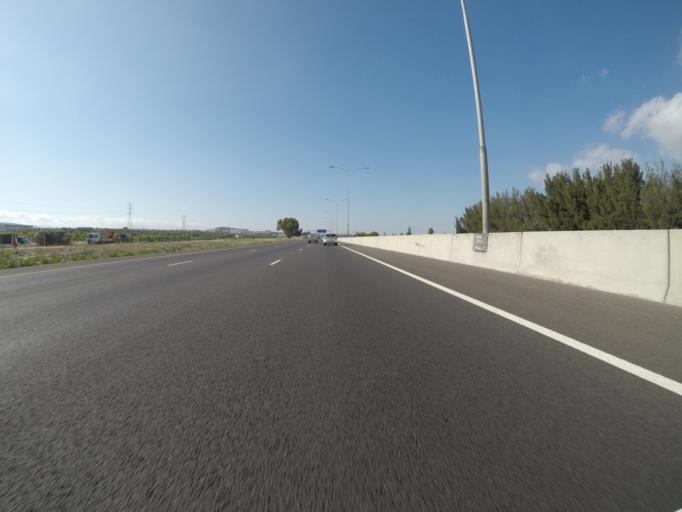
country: ZA
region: Western Cape
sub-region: City of Cape Town
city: Kraaifontein
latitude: -33.9259
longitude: 18.6631
